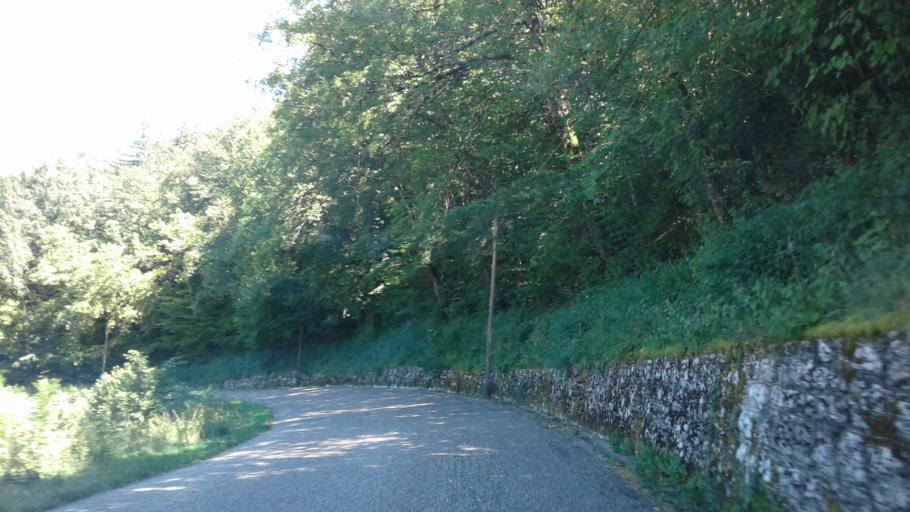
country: FR
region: Rhone-Alpes
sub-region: Departement de l'Ain
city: Artemare
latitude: 45.8745
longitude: 5.6752
